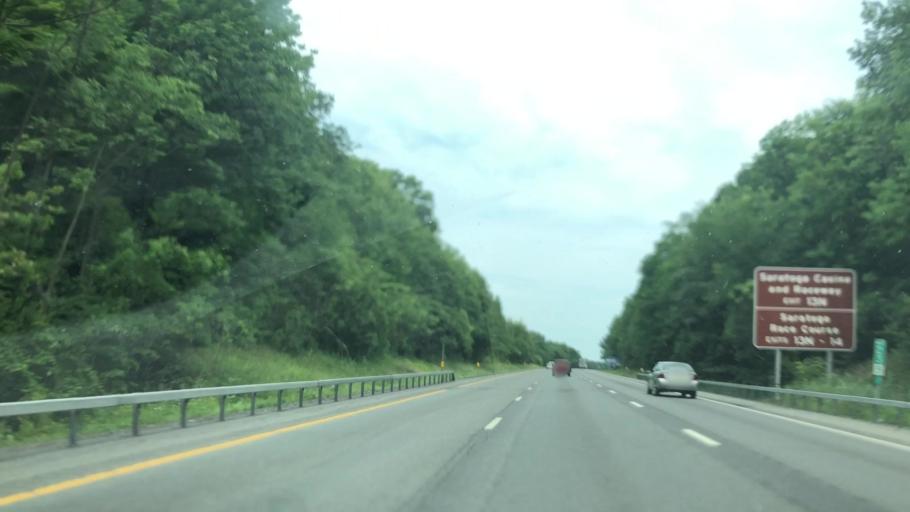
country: US
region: New York
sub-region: Saratoga County
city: Ballston Spa
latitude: 43.0060
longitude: -73.8015
